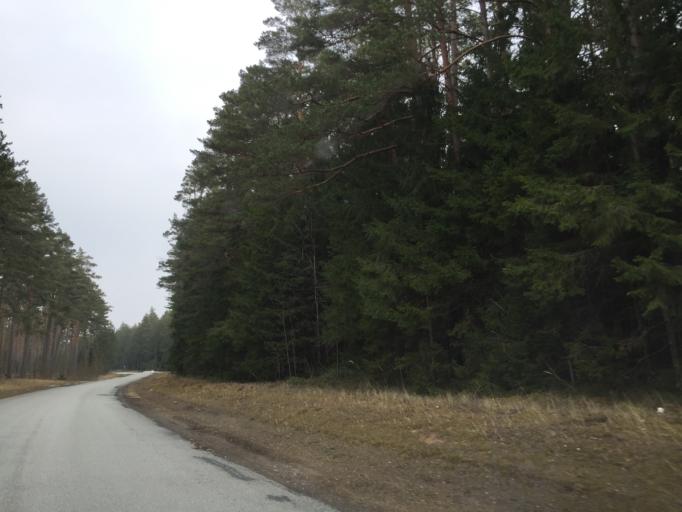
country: LV
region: Salacgrivas
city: Ainazi
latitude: 57.9849
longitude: 24.4195
